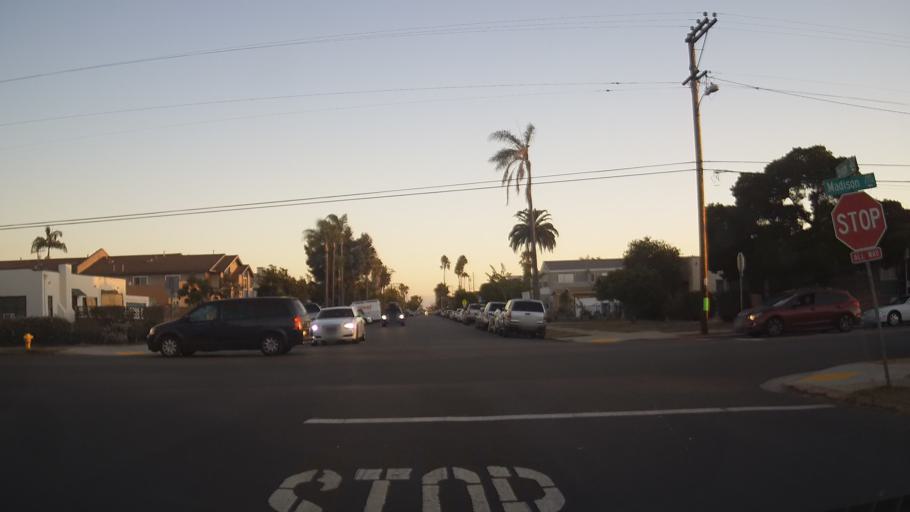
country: US
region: California
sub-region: San Diego County
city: San Diego
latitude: 32.7612
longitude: -117.1352
